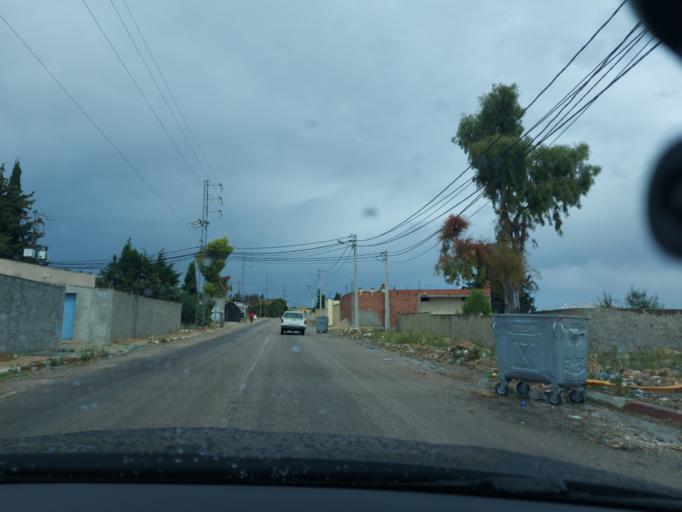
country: TN
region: Silyanah
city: Maktar
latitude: 35.8525
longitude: 9.2150
